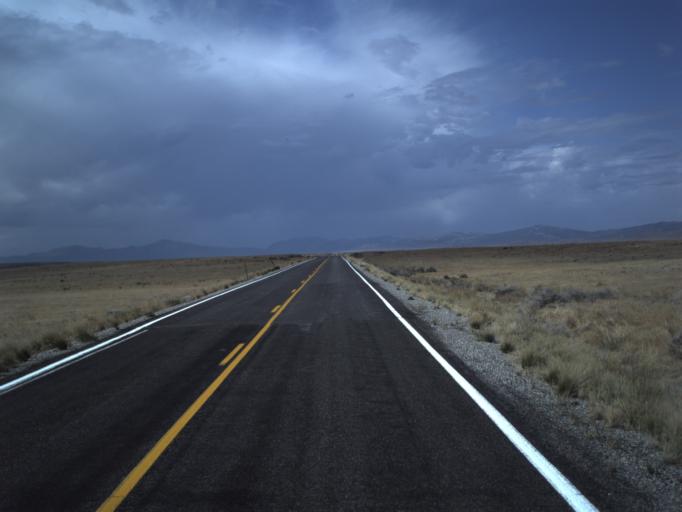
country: US
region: Utah
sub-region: Tooele County
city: Wendover
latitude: 41.3776
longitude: -114.0051
